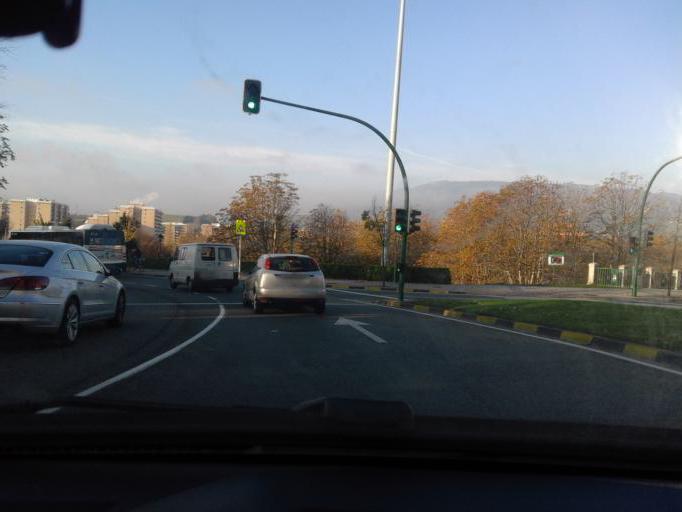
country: ES
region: Navarre
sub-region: Provincia de Navarra
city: Ermitagana
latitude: 42.8159
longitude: -1.6662
